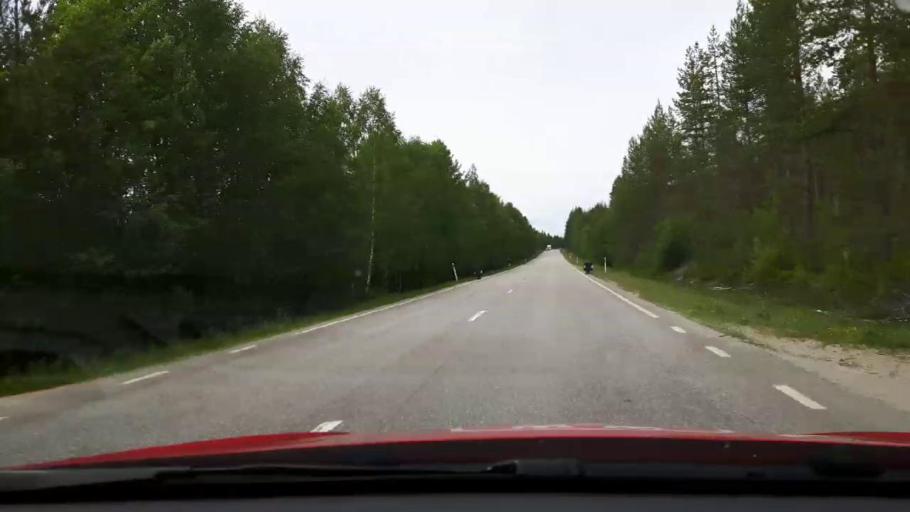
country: SE
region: Jaemtland
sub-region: Harjedalens Kommun
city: Sveg
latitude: 62.0991
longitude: 14.2224
